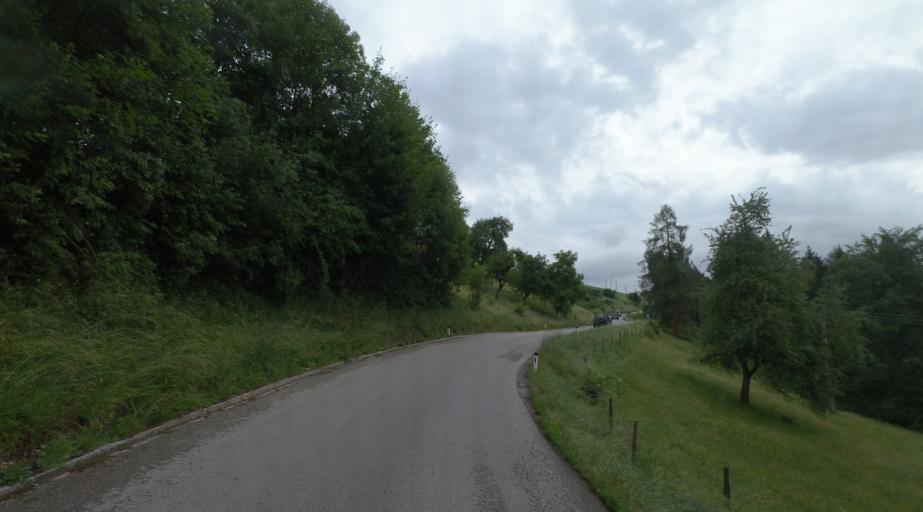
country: AT
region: Upper Austria
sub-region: Politischer Bezirk Kirchdorf an der Krems
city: Micheldorf in Oberoesterreich
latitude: 47.9210
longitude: 14.1542
